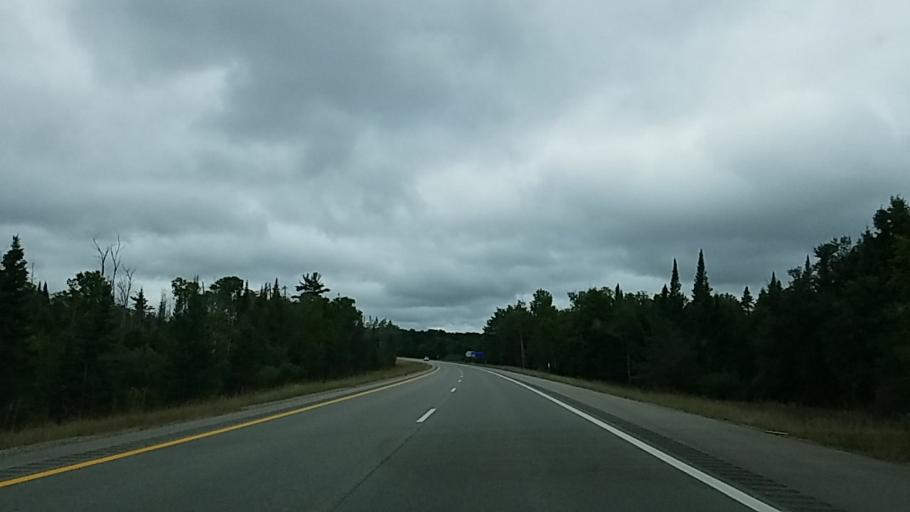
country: US
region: Michigan
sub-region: Otsego County
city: Gaylord
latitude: 45.1611
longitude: -84.6631
